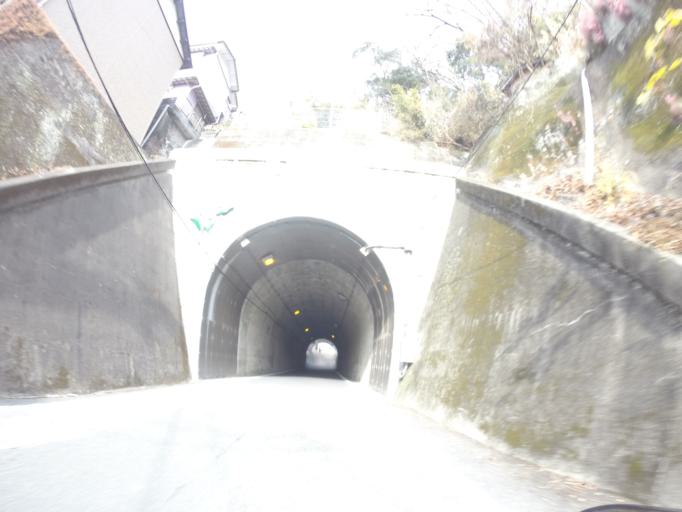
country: JP
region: Shizuoka
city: Heda
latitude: 34.8050
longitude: 138.7641
